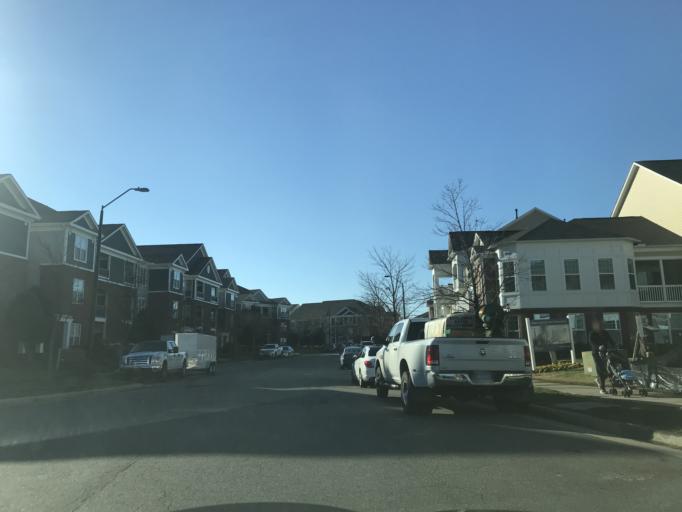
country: US
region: North Carolina
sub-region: Wake County
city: Morrisville
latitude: 35.8982
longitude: -78.7953
